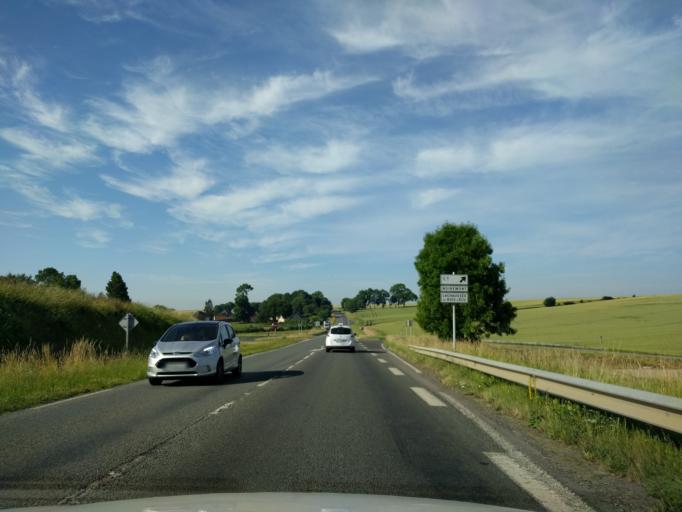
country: FR
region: Picardie
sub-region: Departement de l'Oise
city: Breteuil
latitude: 49.5524
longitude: 2.2079
